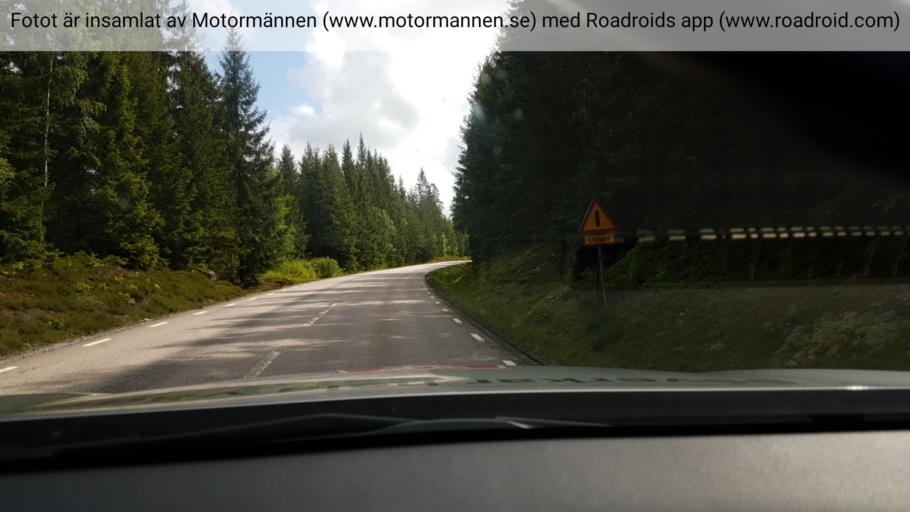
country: SE
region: Vaestra Goetaland
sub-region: Marks Kommun
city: Fritsla
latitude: 57.5009
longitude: 12.9224
